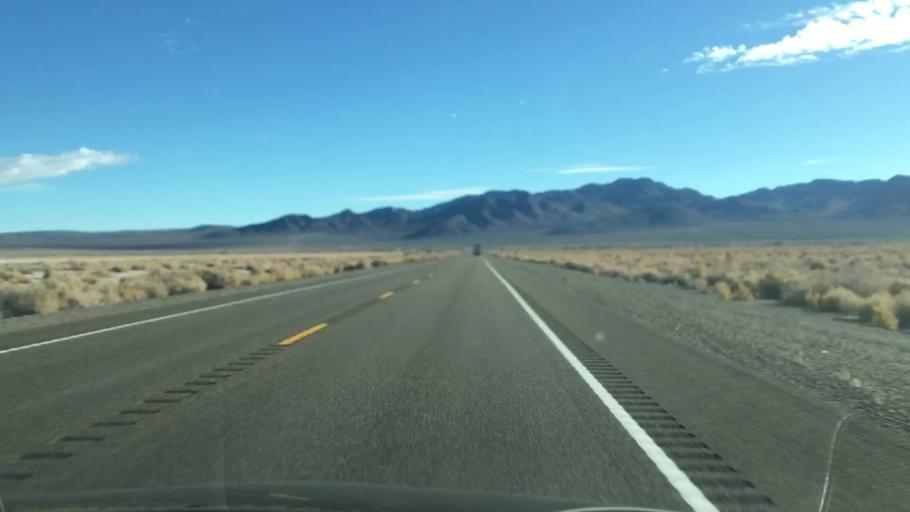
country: US
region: Nevada
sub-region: Mineral County
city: Hawthorne
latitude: 38.2804
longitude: -118.1006
